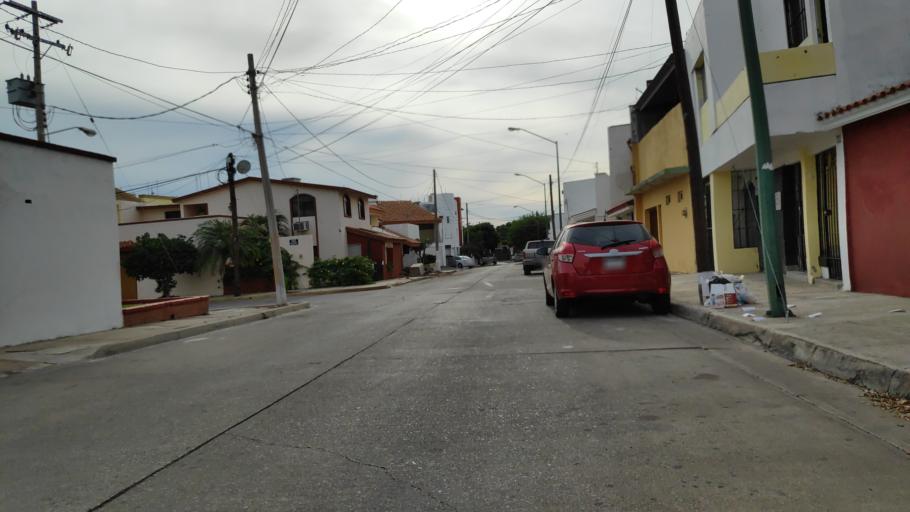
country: MX
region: Sinaloa
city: Culiacan
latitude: 24.7948
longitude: -107.3983
